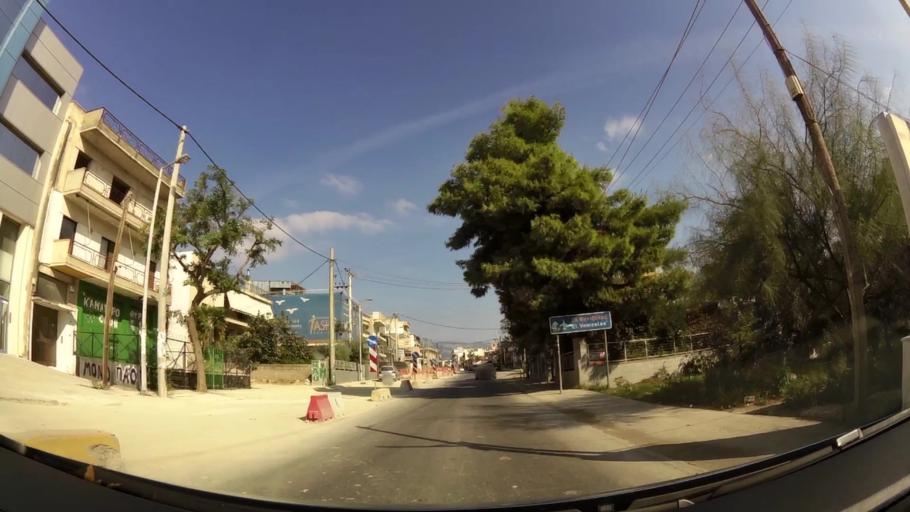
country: GR
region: Attica
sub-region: Nomarchia Athinas
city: Kamateron
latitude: 38.0565
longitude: 23.7134
